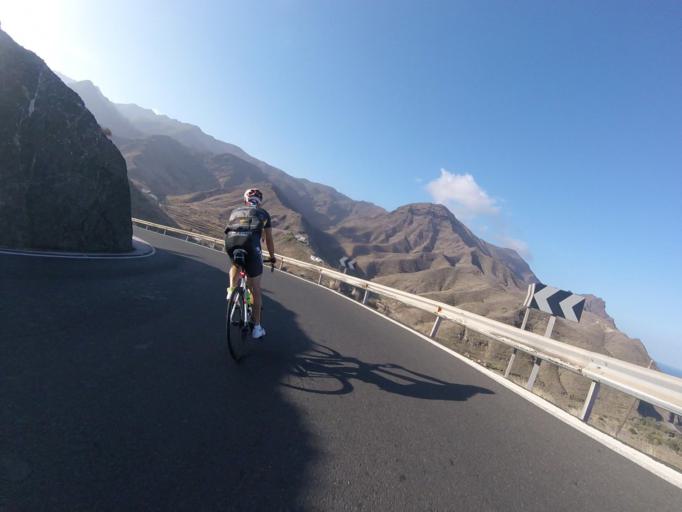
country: ES
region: Canary Islands
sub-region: Provincia de Las Palmas
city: Agaete
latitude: 28.0538
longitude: -15.7334
